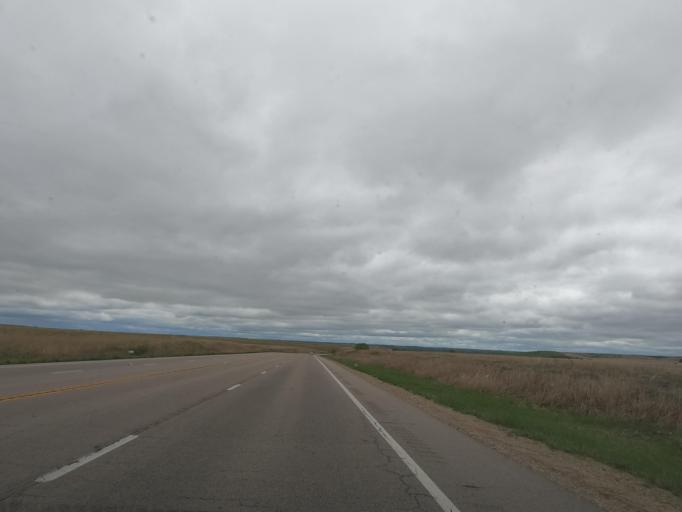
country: US
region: Kansas
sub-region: Greenwood County
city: Eureka
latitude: 37.6436
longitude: -96.4274
